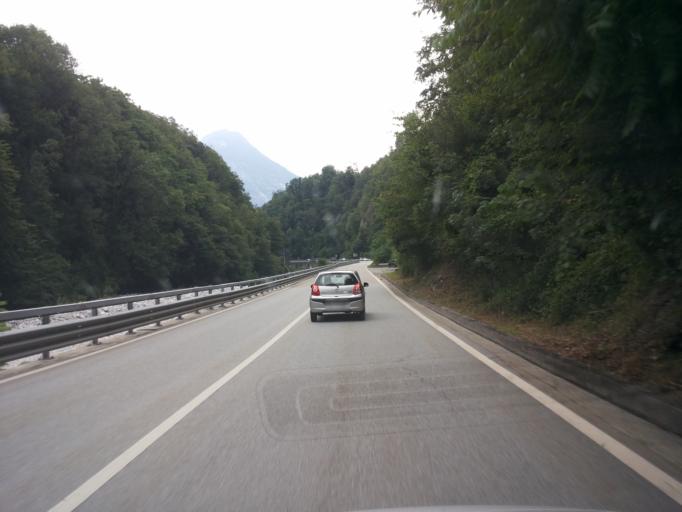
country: IT
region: Piedmont
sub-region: Provincia Verbano-Cusio-Ossola
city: Trontano
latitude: 46.1292
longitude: 8.3338
